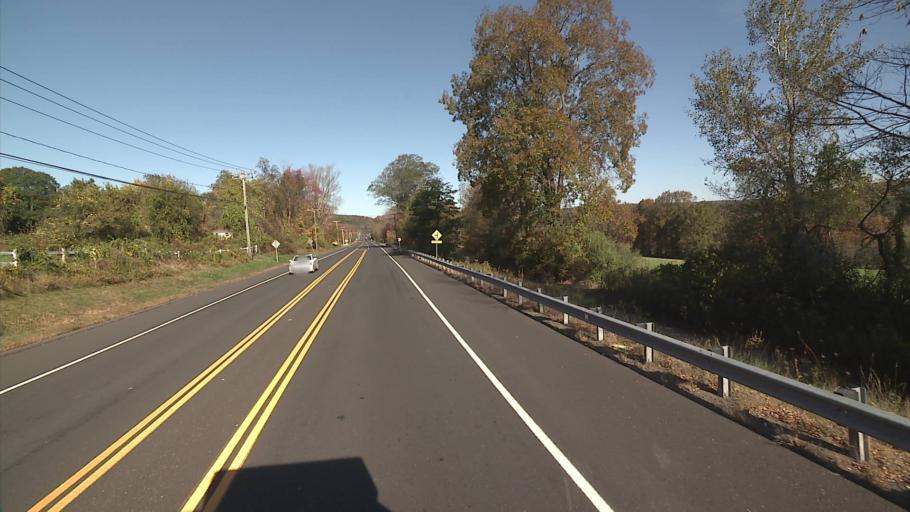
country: US
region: Connecticut
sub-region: Tolland County
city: Coventry Lake
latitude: 41.7500
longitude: -72.3957
